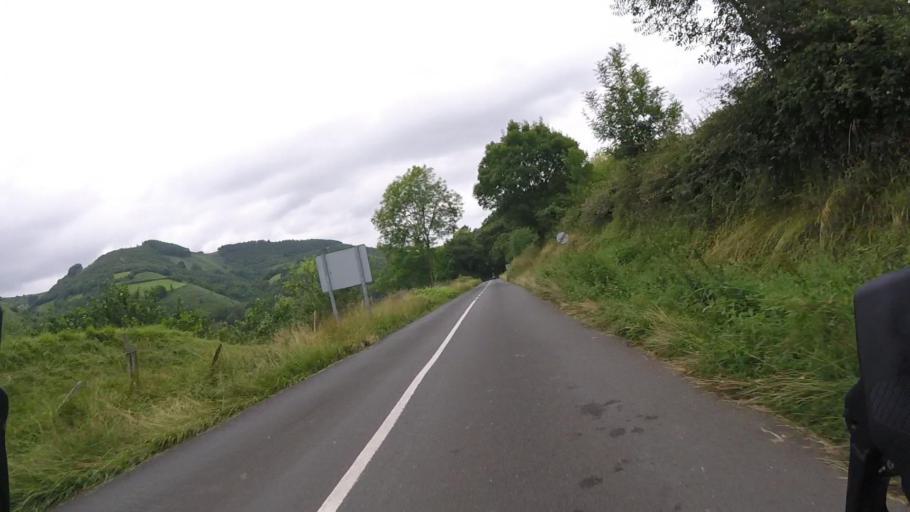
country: ES
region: Basque Country
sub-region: Provincia de Guipuzcoa
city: Irun
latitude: 43.2718
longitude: -1.8149
